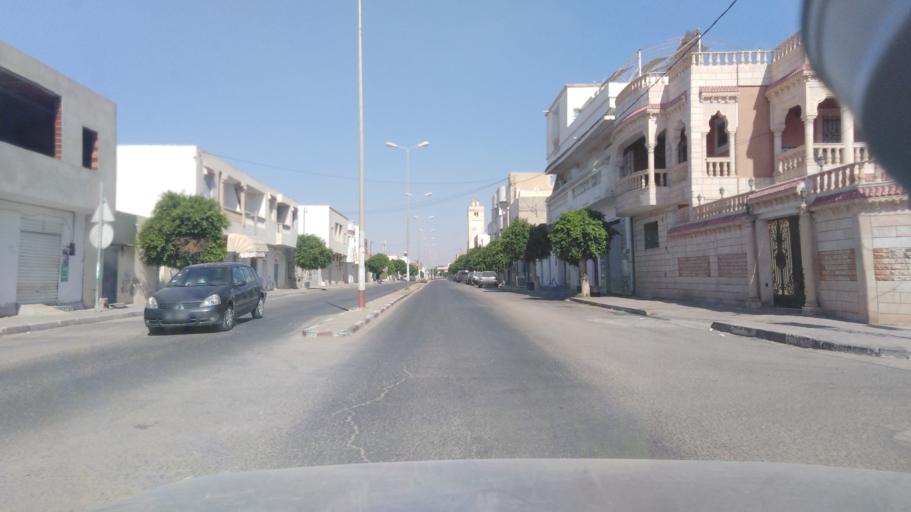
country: TN
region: Qabis
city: Gabes
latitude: 33.9598
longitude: 9.9992
